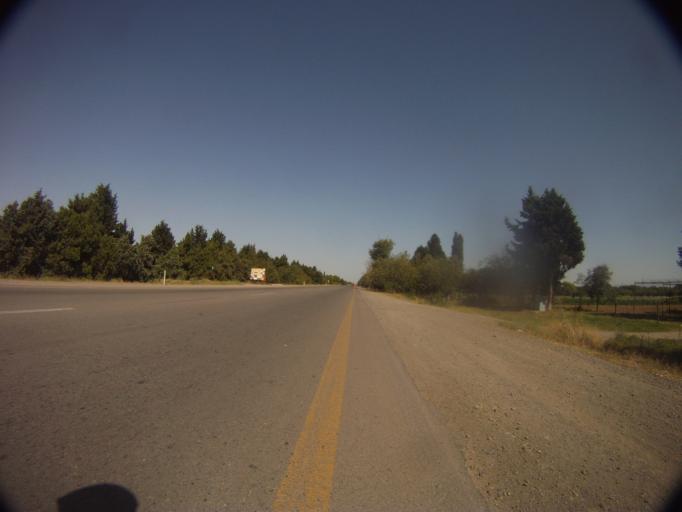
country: AZ
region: Shamkir Rayon
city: Dzagam
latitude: 40.9025
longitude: 45.9624
